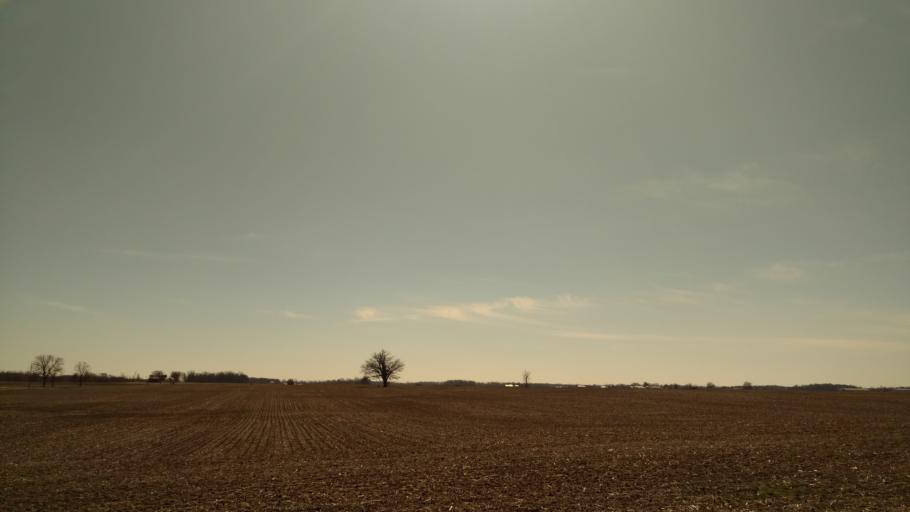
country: US
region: Ohio
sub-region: Union County
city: Richwood
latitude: 40.5135
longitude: -83.3723
